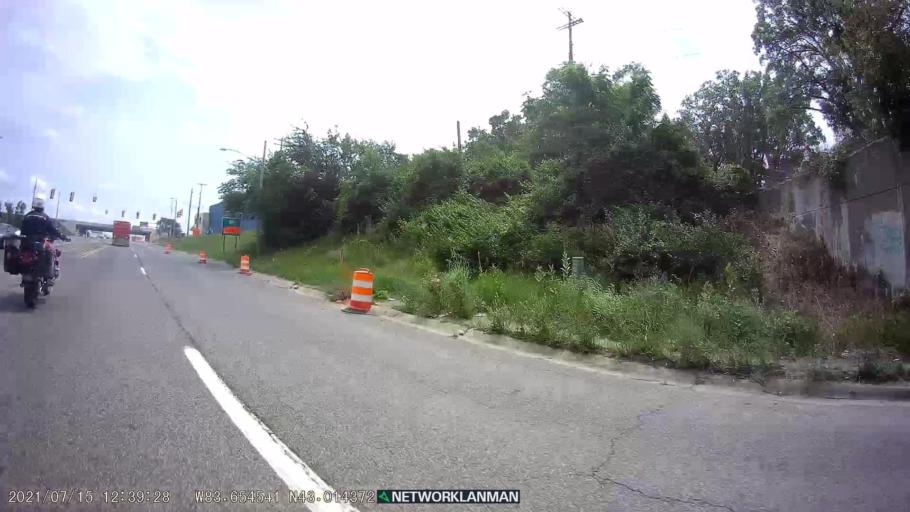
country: US
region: Michigan
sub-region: Genesee County
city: Flint
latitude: 43.0142
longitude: -83.6545
